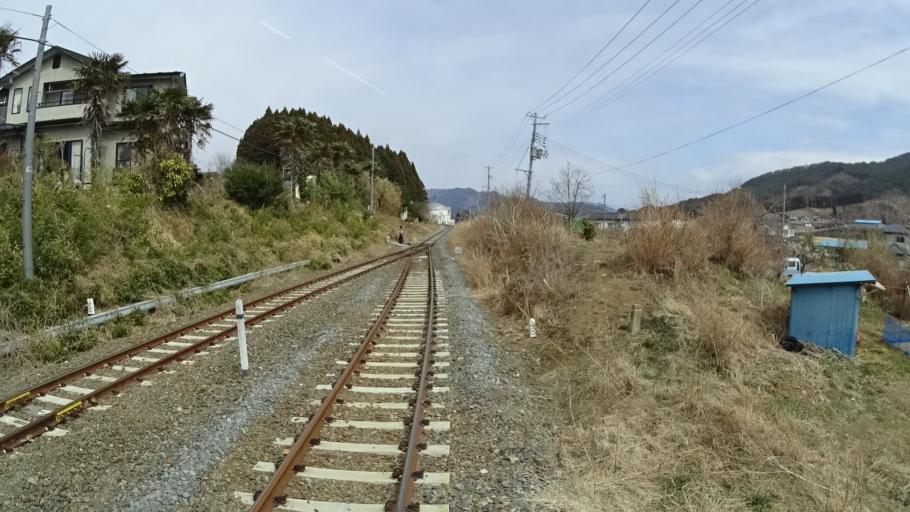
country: JP
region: Iwate
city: Yamada
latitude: 39.4326
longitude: 141.9745
